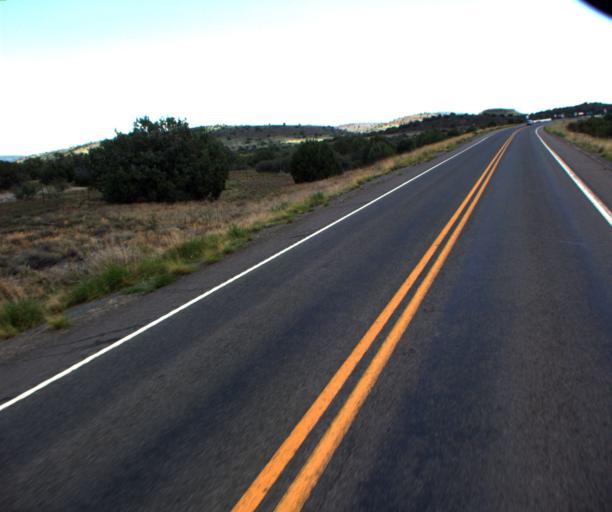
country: US
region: Arizona
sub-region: Yavapai County
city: Camp Verde
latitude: 34.5148
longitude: -111.9976
